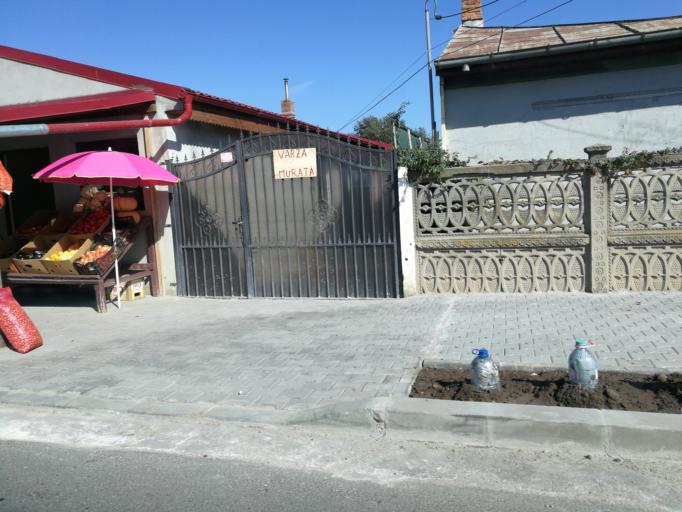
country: RO
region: Ilfov
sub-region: Comuna Dragomiresti-Vale
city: Dragomiresti-Deal
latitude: 44.4608
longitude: 25.9447
